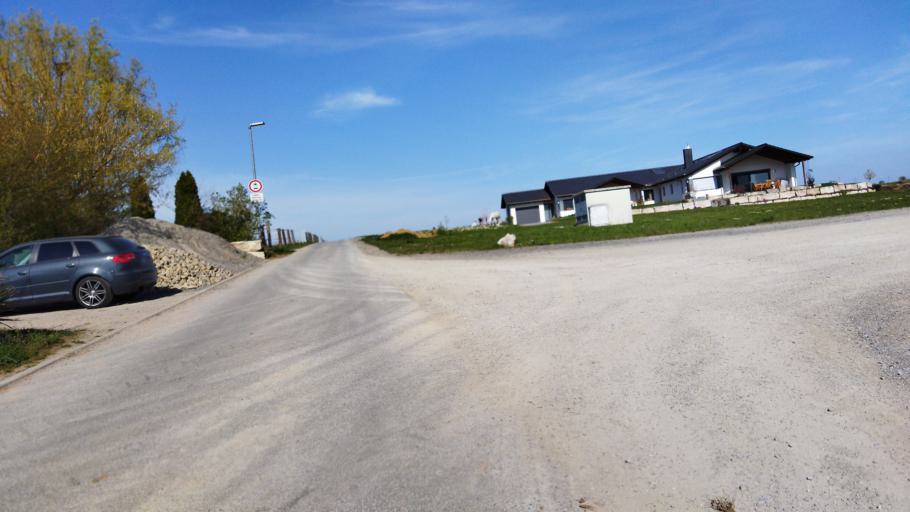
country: DE
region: Baden-Wuerttemberg
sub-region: Regierungsbezirk Stuttgart
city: Freudental
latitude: 48.9808
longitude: 9.0506
